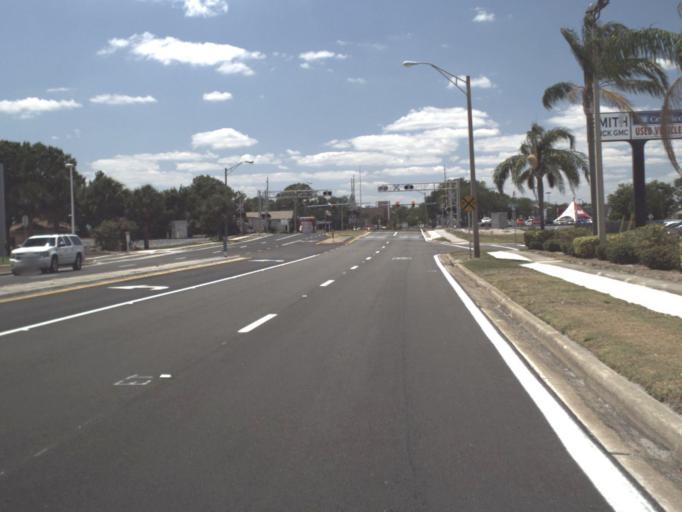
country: US
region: Florida
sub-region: Brevard County
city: Melbourne
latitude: 28.0931
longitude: -80.6129
